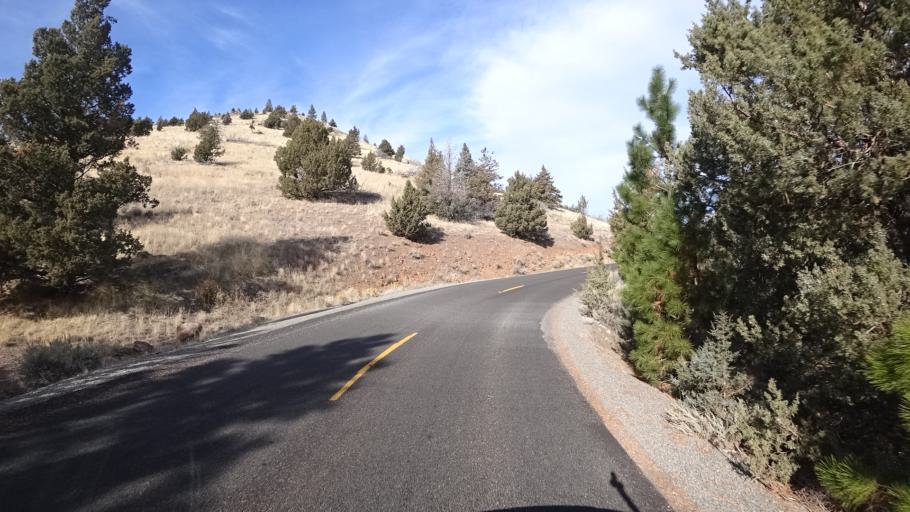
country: US
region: California
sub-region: Siskiyou County
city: Weed
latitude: 41.4991
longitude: -122.3900
